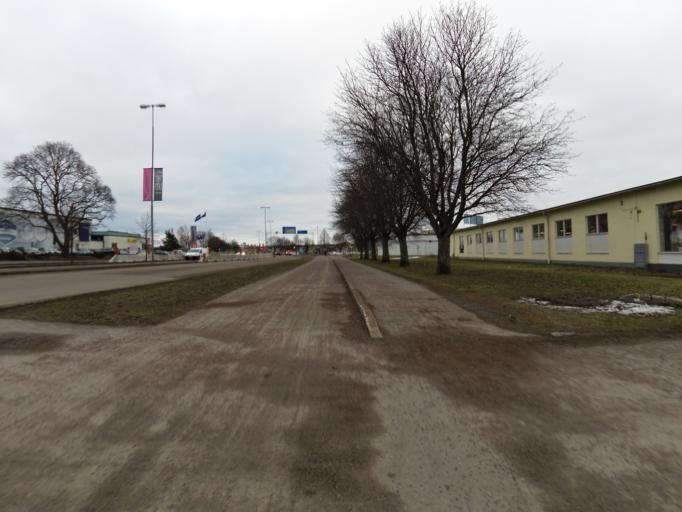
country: SE
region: Gaevleborg
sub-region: Gavle Kommun
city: Gavle
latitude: 60.6626
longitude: 17.1560
